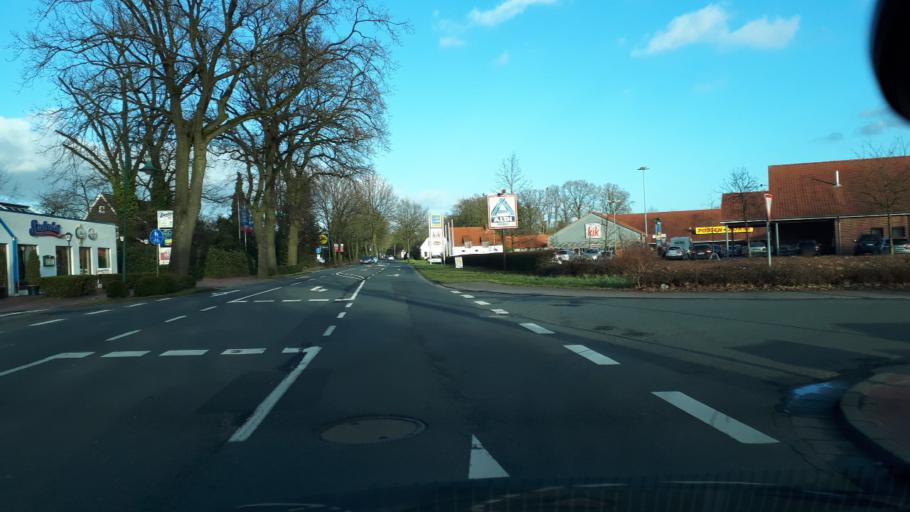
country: DE
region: Lower Saxony
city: Molbergen
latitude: 52.8577
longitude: 7.9276
